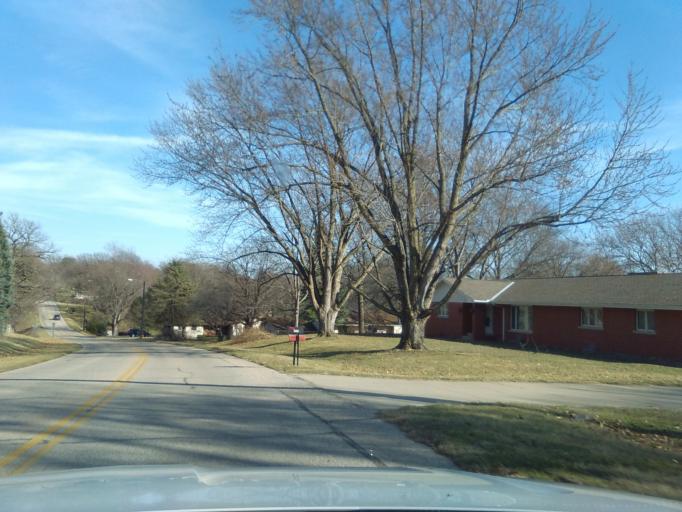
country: US
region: Nebraska
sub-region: Otoe County
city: Nebraska City
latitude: 40.6789
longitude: -95.8776
